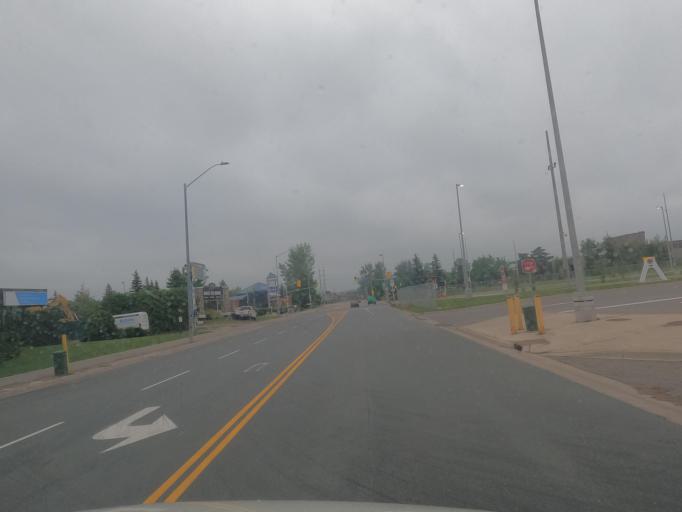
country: CA
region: Ontario
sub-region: Algoma
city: Sault Ste. Marie
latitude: 46.5193
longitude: -84.3478
